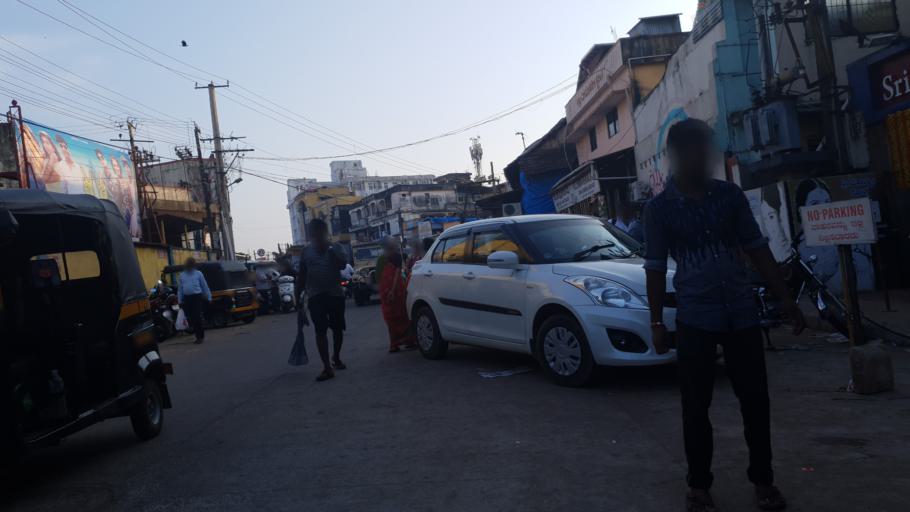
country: IN
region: Karnataka
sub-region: Dakshina Kannada
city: Mangalore
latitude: 12.8674
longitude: 74.8384
